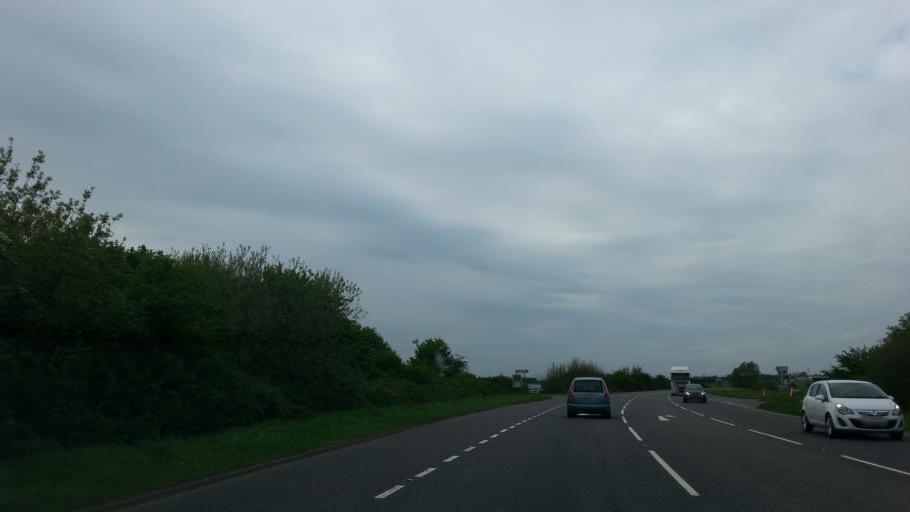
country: GB
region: England
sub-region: Cambridgeshire
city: March
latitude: 52.5330
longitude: 0.0700
